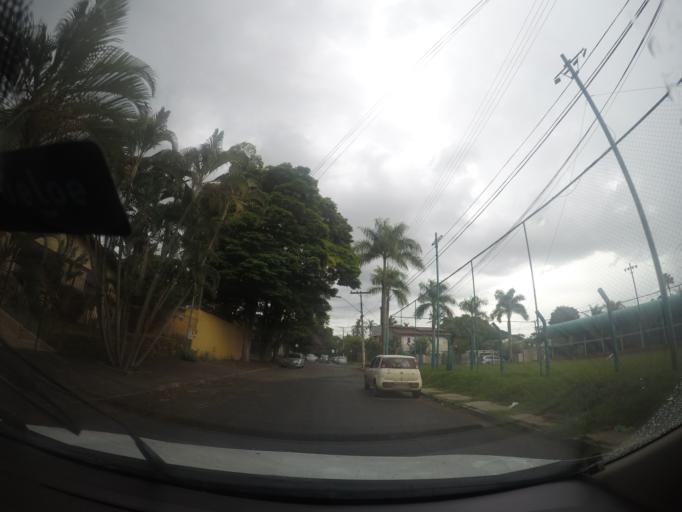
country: BR
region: Goias
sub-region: Goiania
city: Goiania
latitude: -16.6485
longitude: -49.2373
